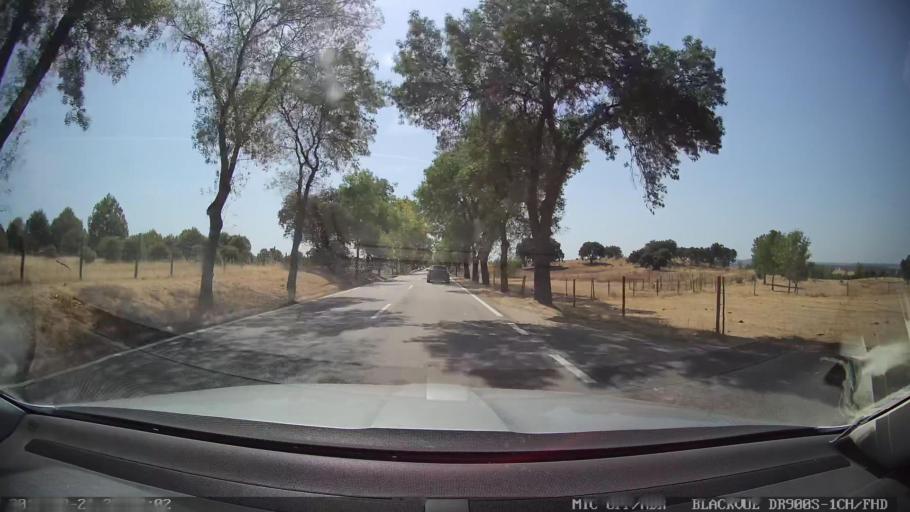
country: PT
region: Castelo Branco
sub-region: Idanha-A-Nova
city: Idanha-a-Nova
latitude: 39.8601
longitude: -7.3157
